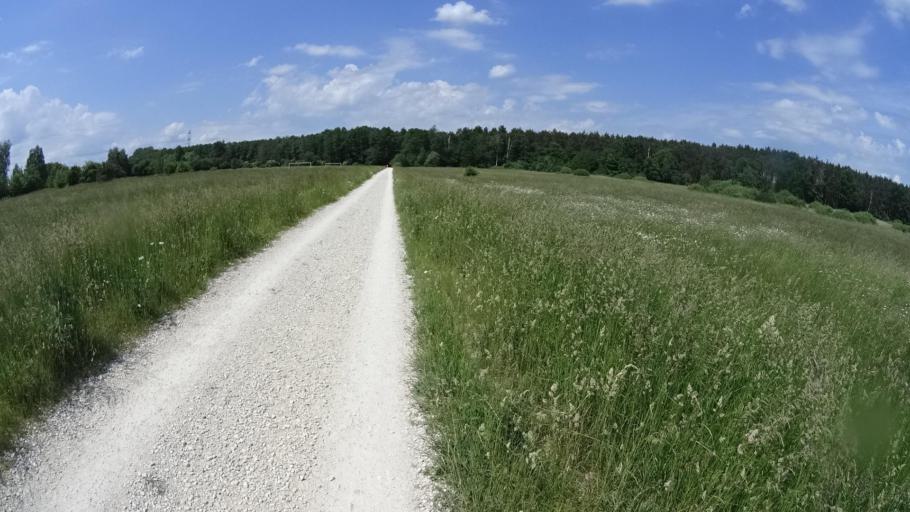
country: PL
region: Masovian Voivodeship
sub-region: Powiat warszawski zachodni
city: Stare Babice
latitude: 52.2695
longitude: 20.8442
